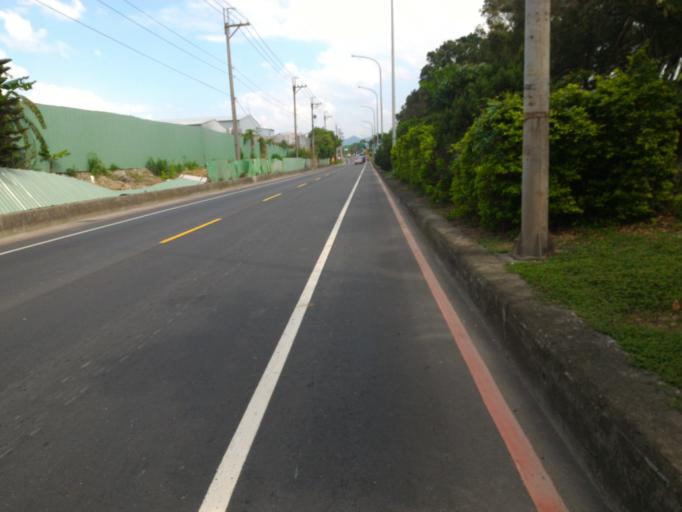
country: TW
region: Taipei
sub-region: Taipei
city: Banqiao
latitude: 24.9693
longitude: 121.4017
